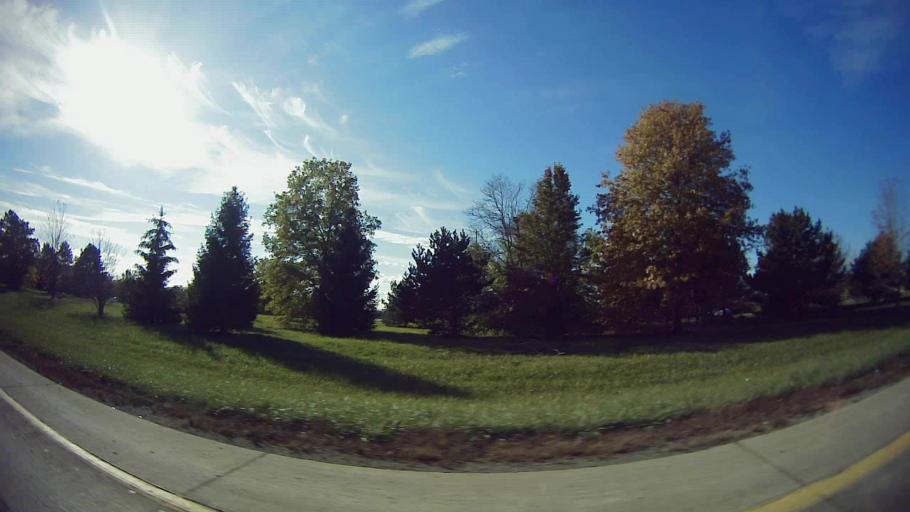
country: US
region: Michigan
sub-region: Wayne County
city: Romulus
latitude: 42.2241
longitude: -83.4096
